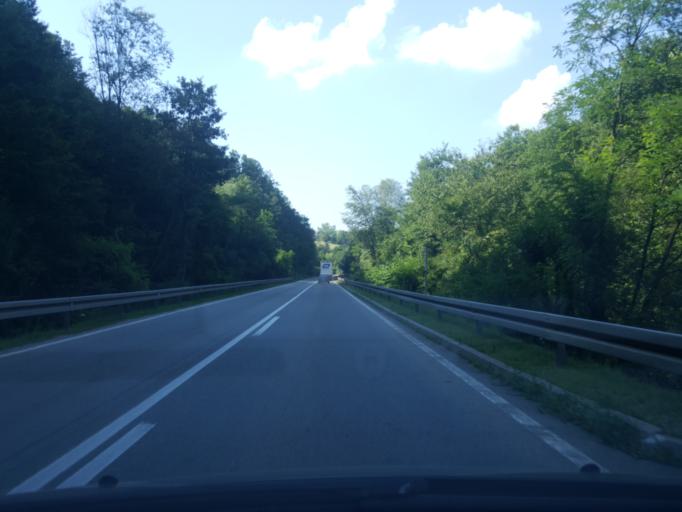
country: RS
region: Central Serbia
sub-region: Moravicki Okrug
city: Gornji Milanovac
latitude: 44.1075
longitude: 20.4835
